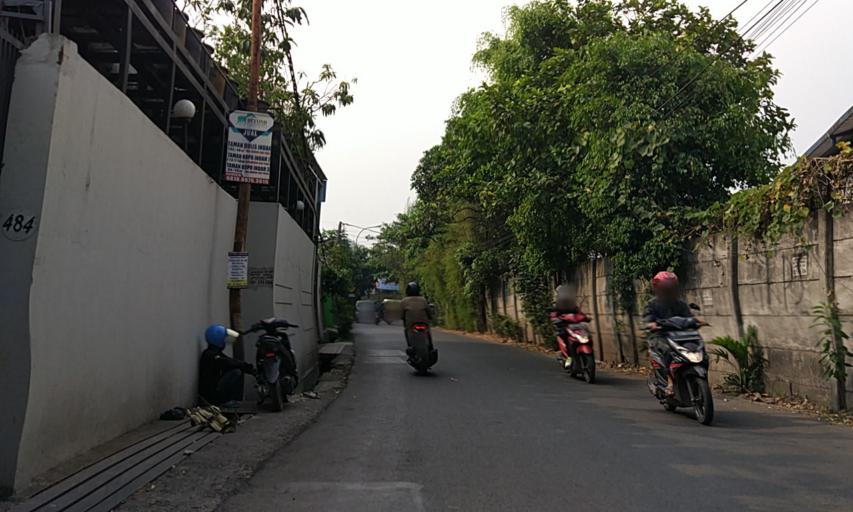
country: ID
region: West Java
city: Margahayukencana
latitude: -6.9433
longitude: 107.5669
